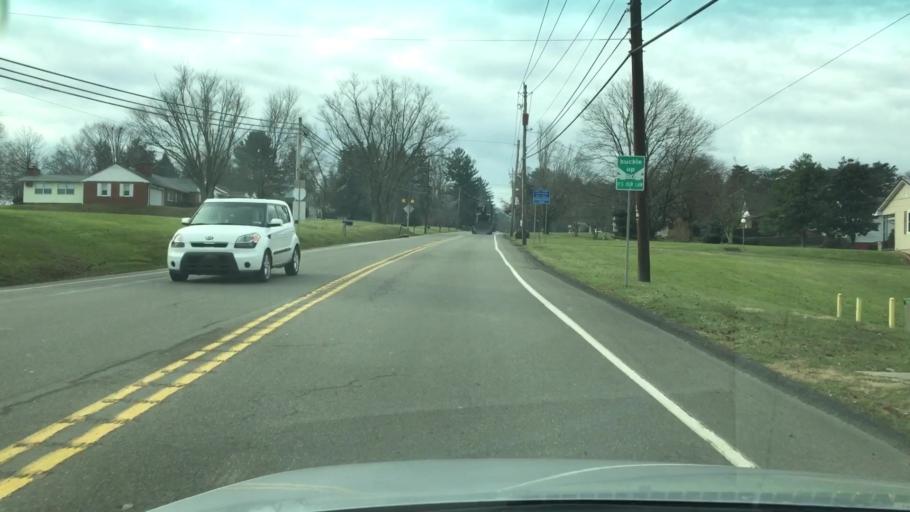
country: US
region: Pennsylvania
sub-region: Columbia County
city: Light Street
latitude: 41.0246
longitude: -76.4287
